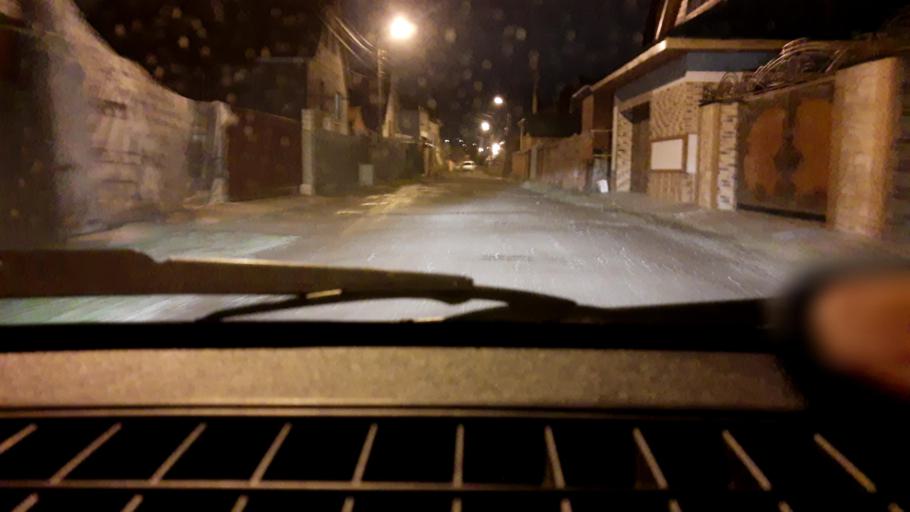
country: RU
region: Bashkortostan
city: Ufa
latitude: 54.7057
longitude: 55.9424
